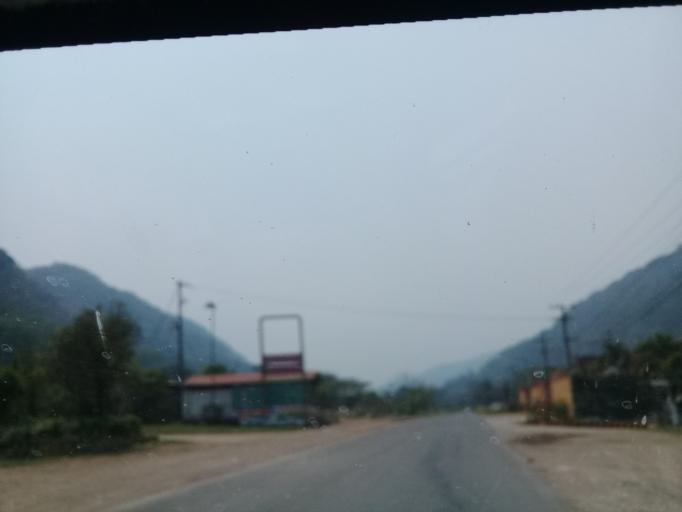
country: MX
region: Veracruz
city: Tezonapa
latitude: 18.6203
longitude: -96.7000
